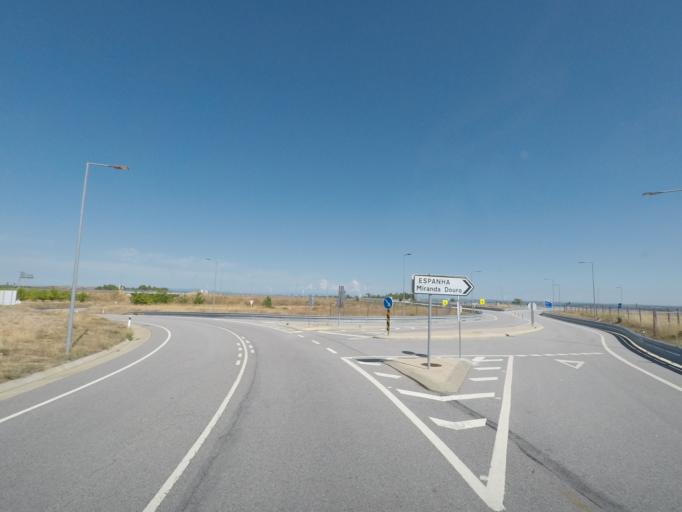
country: ES
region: Castille and Leon
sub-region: Provincia de Salamanca
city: Villarino de los Aires
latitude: 41.3673
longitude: -6.5051
